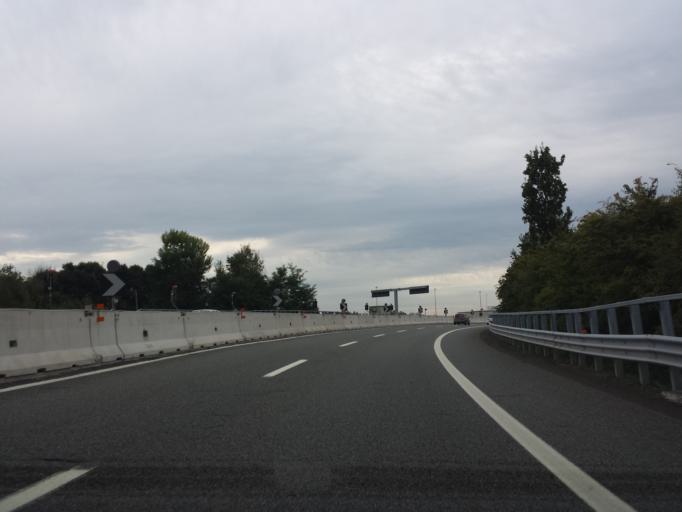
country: IT
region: Lombardy
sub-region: Provincia di Varese
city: Cavaria Con Premezzo
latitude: 45.6758
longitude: 8.8005
